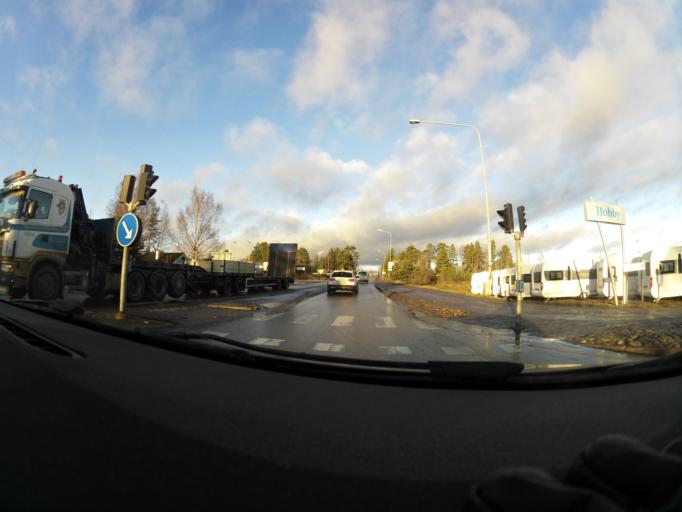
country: SE
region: Gaevleborg
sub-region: Gavle Kommun
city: Valbo
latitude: 60.6479
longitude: 17.0195
